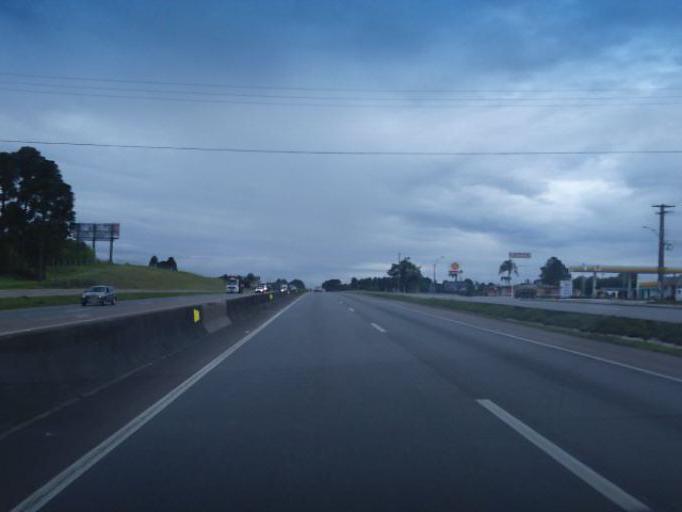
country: BR
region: Parana
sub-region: Sao Jose Dos Pinhais
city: Sao Jose dos Pinhais
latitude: -25.6742
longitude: -49.1509
